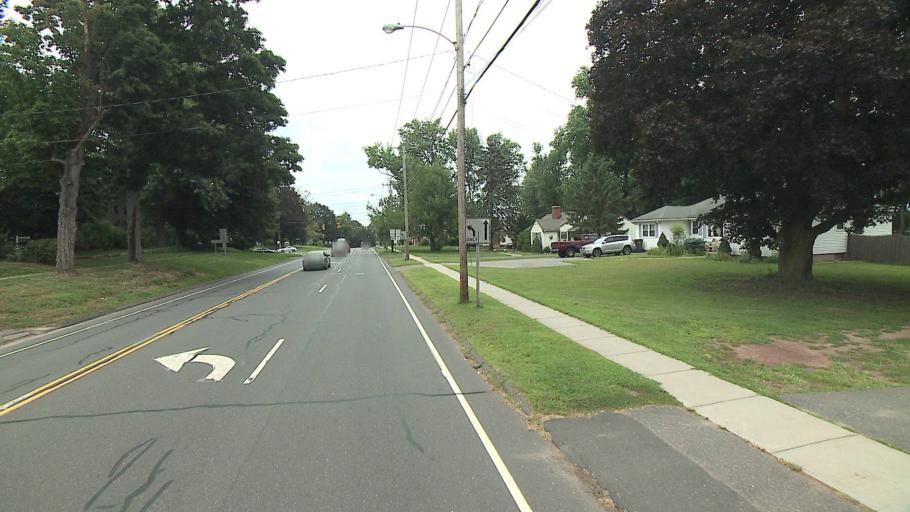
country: US
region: Connecticut
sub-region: Hartford County
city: Wethersfield
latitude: 41.6950
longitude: -72.6593
